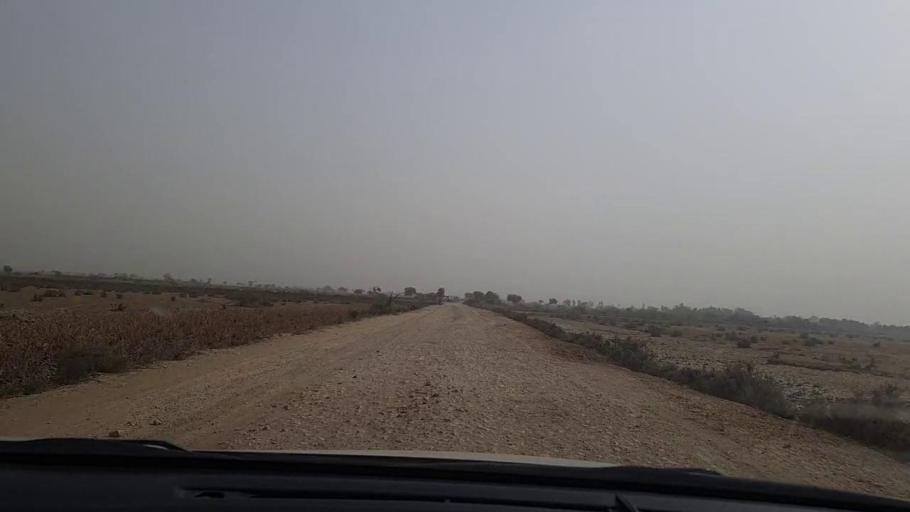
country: PK
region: Sindh
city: Pithoro
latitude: 25.4124
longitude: 69.3172
